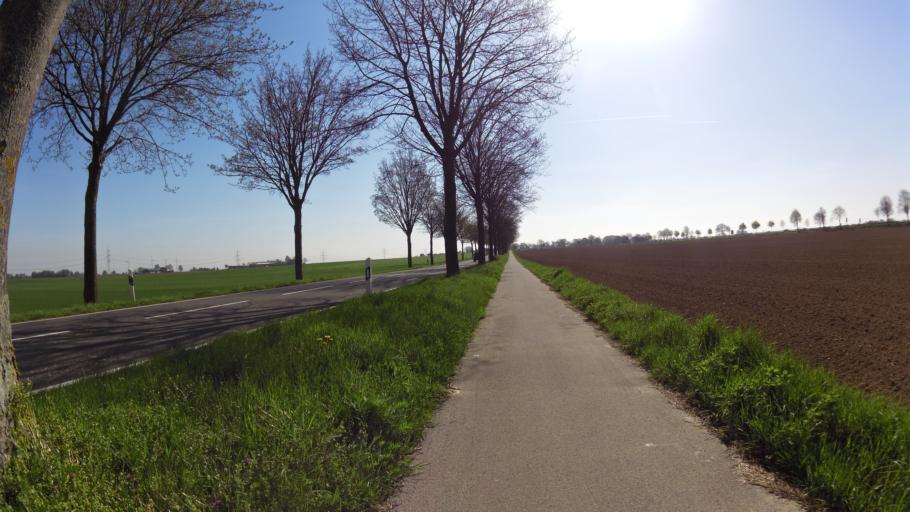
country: DE
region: North Rhine-Westphalia
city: Geilenkirchen
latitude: 50.9564
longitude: 6.1512
